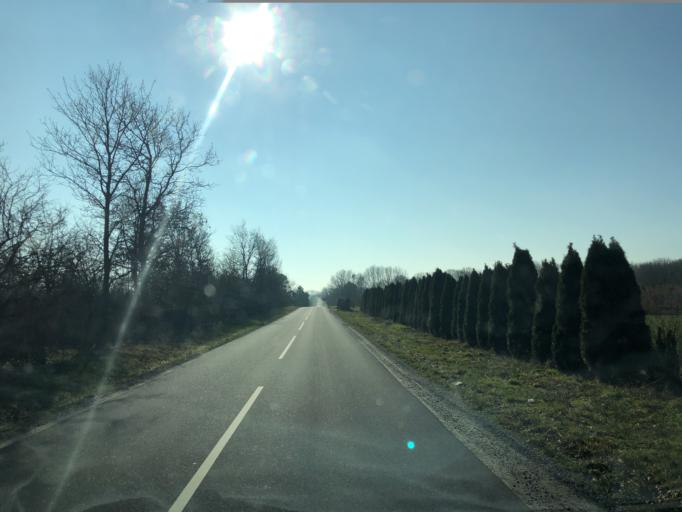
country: DK
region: Central Jutland
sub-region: Ikast-Brande Kommune
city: Bording Kirkeby
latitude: 56.1619
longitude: 9.3300
